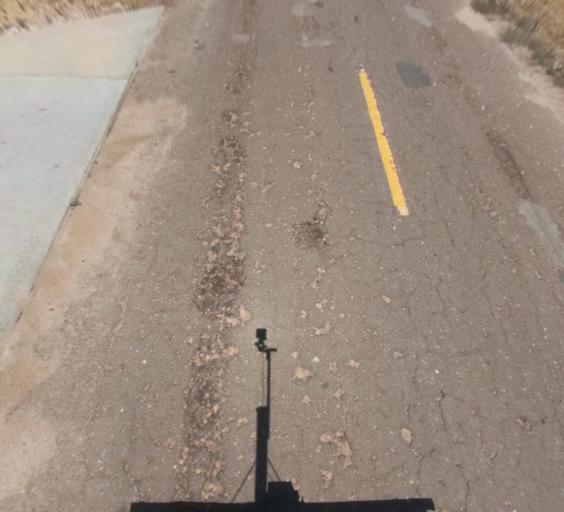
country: US
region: California
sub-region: Madera County
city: Madera Acres
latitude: 37.0353
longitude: -119.9987
